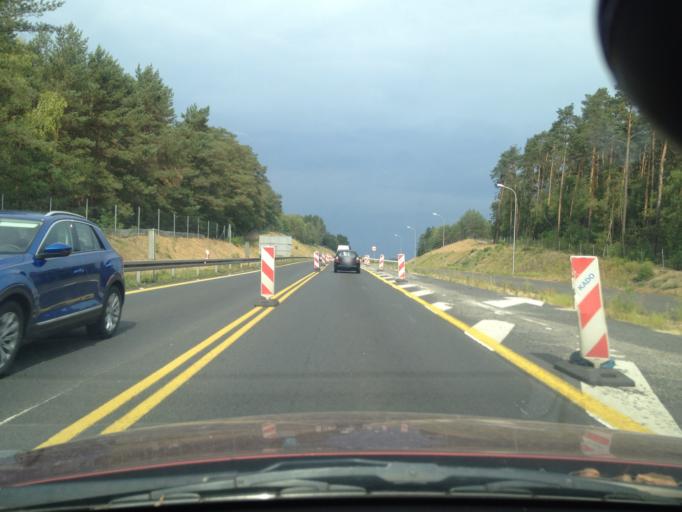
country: PL
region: Lubusz
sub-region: Zielona Gora
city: Zielona Gora
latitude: 51.9272
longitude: 15.5579
